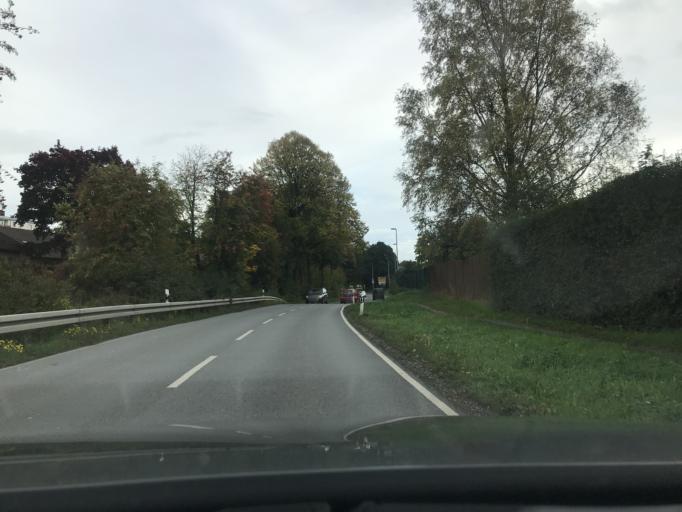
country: DE
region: North Rhine-Westphalia
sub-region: Regierungsbezirk Arnsberg
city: Soest
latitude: 51.5664
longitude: 8.1310
